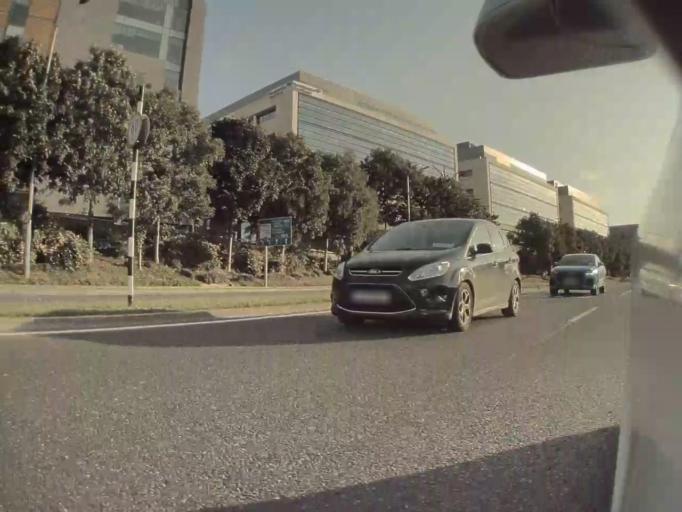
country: IE
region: Leinster
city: Sandyford
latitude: 53.2718
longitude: -6.2030
